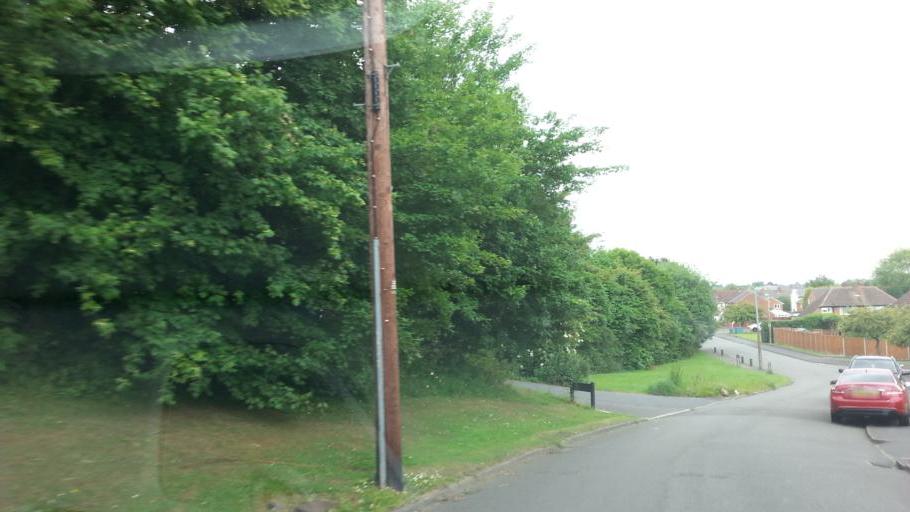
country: GB
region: England
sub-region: Sandwell
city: Tipton
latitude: 52.5304
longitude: -2.0914
